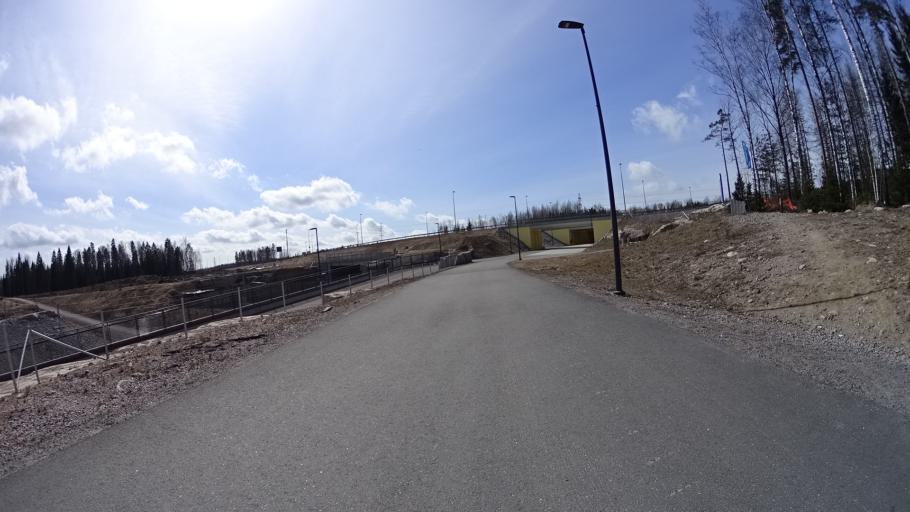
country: FI
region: Uusimaa
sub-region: Helsinki
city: Kilo
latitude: 60.3137
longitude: 24.8442
